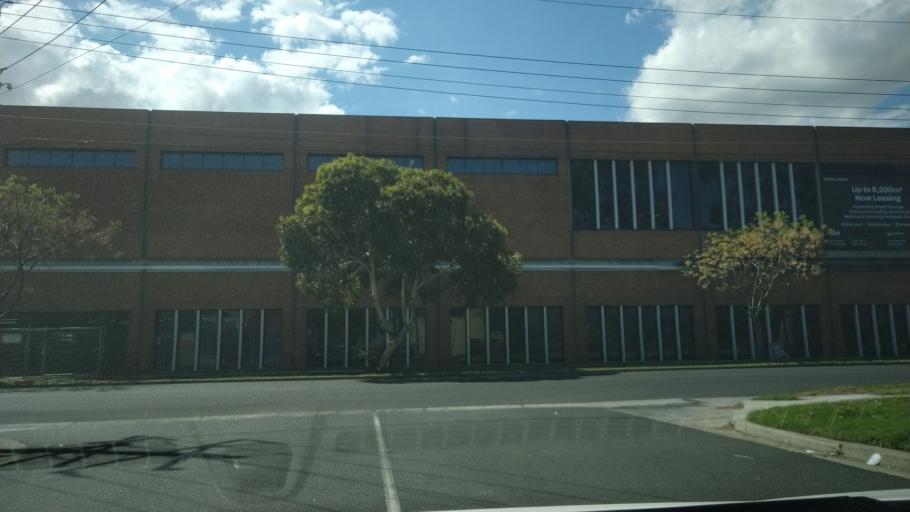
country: AU
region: Victoria
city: Highett
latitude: -37.9424
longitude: 145.0628
